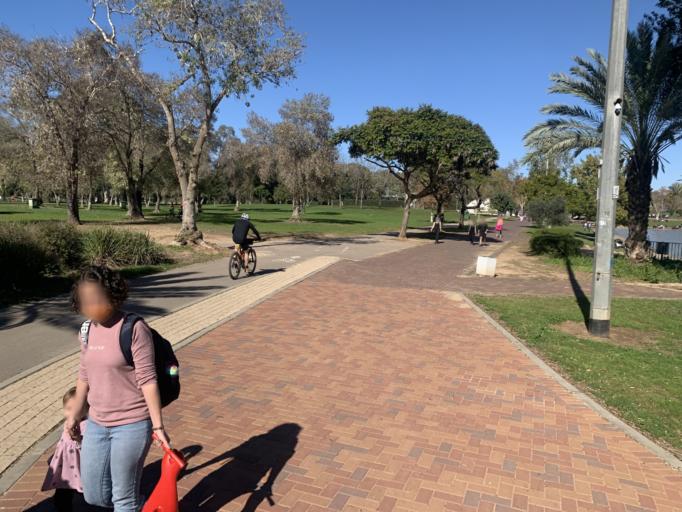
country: IL
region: Tel Aviv
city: Ramat Gan
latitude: 32.0970
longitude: 34.8094
